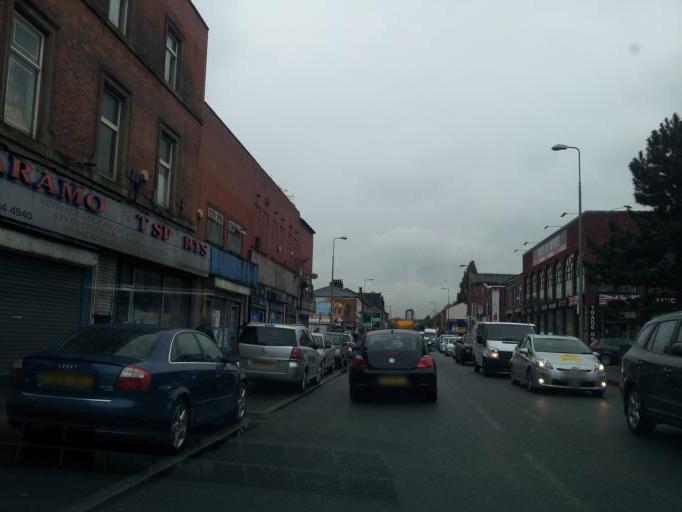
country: GB
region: England
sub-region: Manchester
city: Cheetham Hill
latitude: 53.4926
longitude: -2.2492
